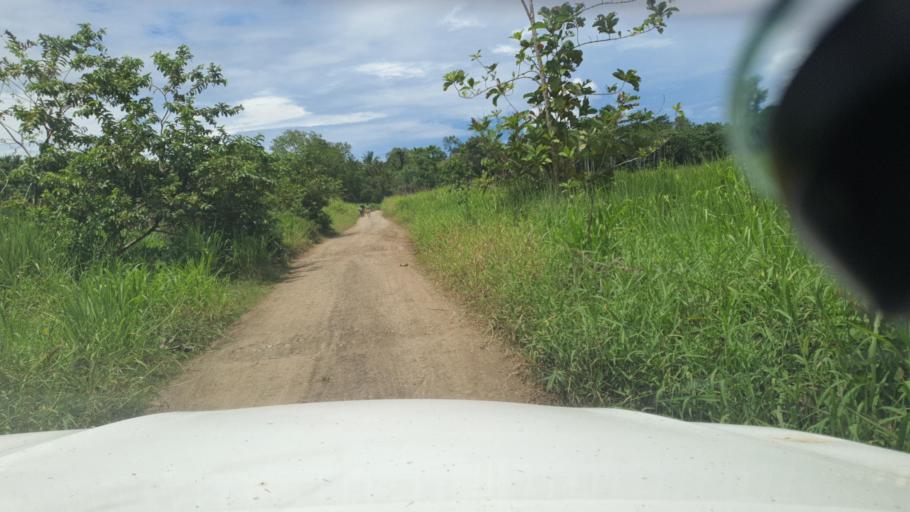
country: SB
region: Guadalcanal
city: Honiara
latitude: -9.4878
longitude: 160.3409
